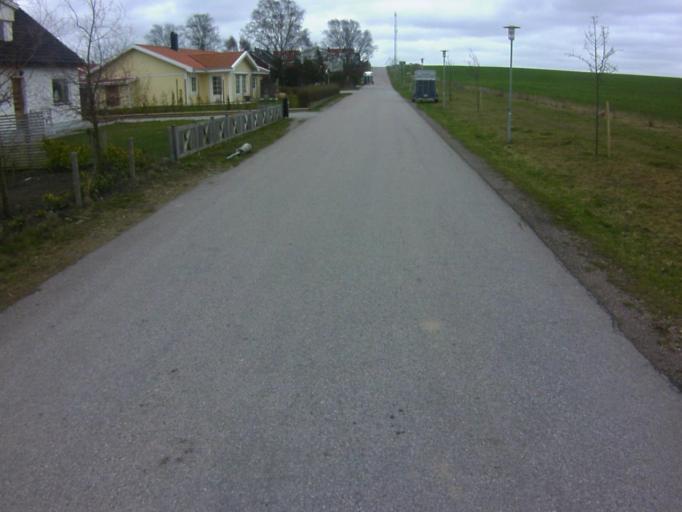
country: SE
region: Skane
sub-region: Kavlinge Kommun
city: Kaevlinge
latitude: 55.7679
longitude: 13.0762
